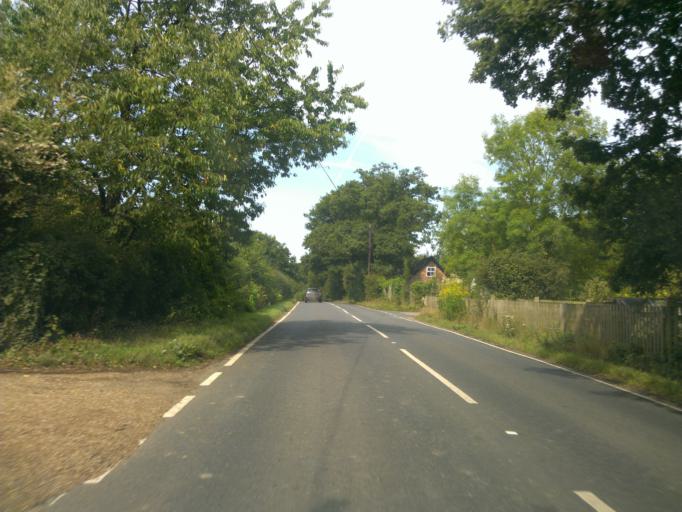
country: GB
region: England
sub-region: Kent
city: Sevenoaks
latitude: 51.2003
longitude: 0.1620
